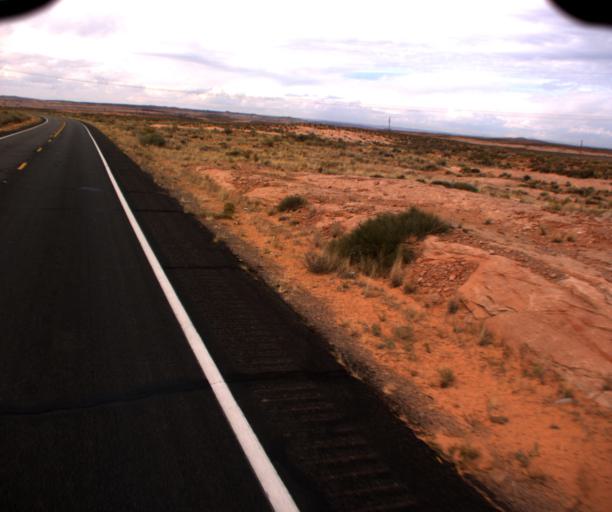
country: US
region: Arizona
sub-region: Apache County
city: Many Farms
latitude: 36.9384
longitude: -109.6382
